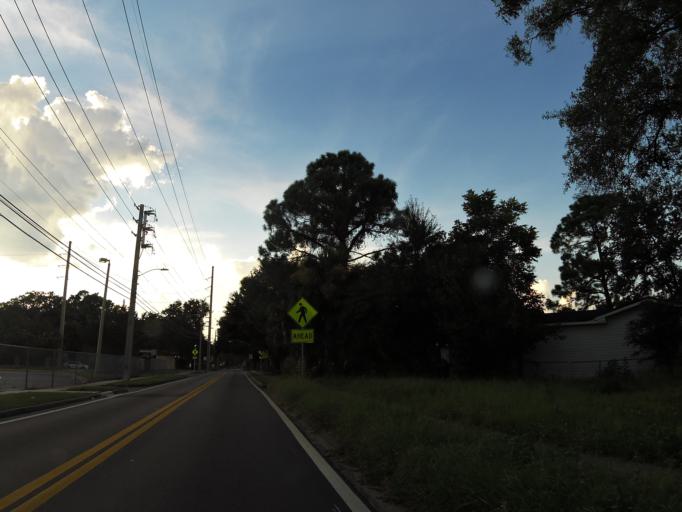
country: US
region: Florida
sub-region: Duval County
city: Jacksonville
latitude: 30.3381
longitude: -81.6855
